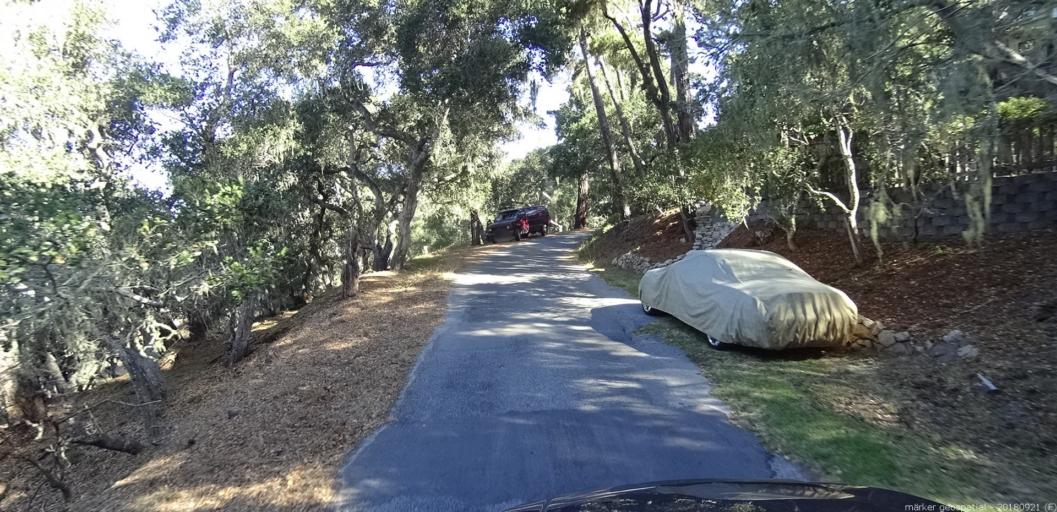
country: US
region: California
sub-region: Monterey County
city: Carmel-by-the-Sea
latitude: 36.5658
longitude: -121.9205
